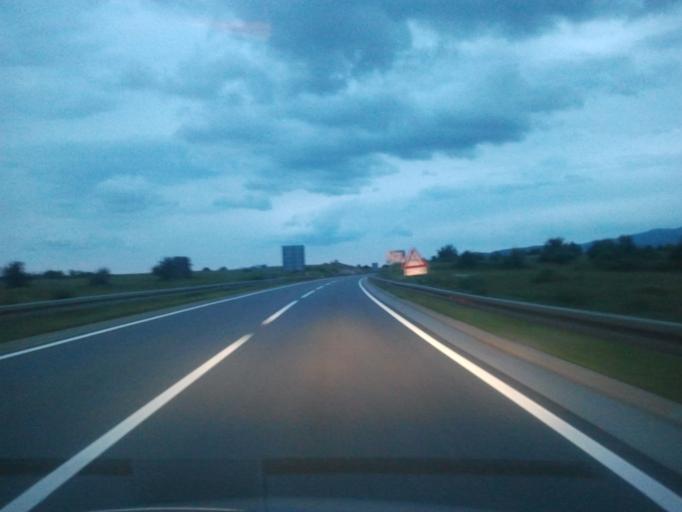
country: HR
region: Zadarska
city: Gracac
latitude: 44.5132
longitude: 15.7446
